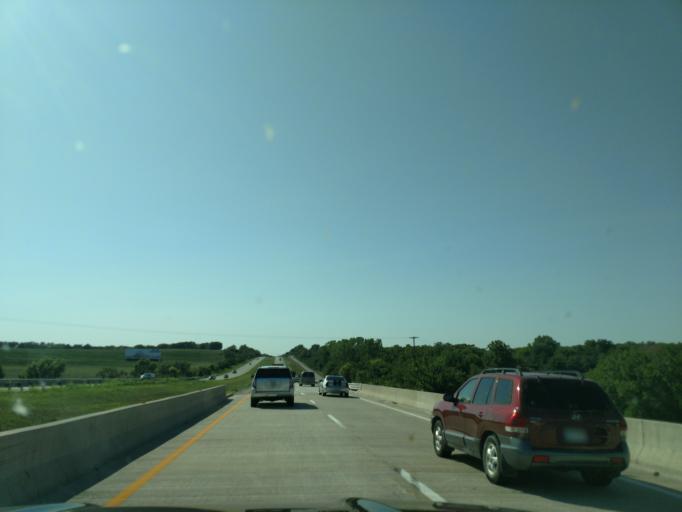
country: US
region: Missouri
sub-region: Andrew County
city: Country Club Village
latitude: 39.8720
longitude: -94.8331
